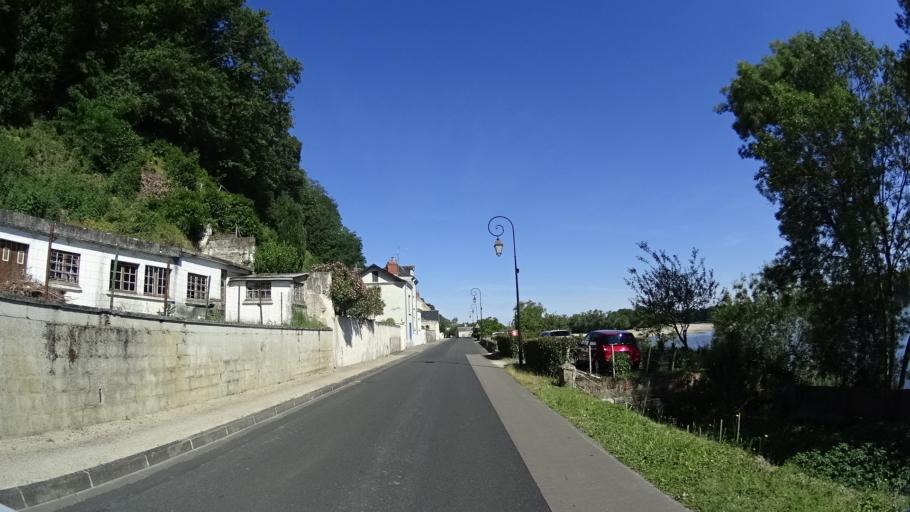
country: FR
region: Pays de la Loire
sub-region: Departement de Maine-et-Loire
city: Saint-Martin-de-la-Place
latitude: 47.3063
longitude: -0.1499
